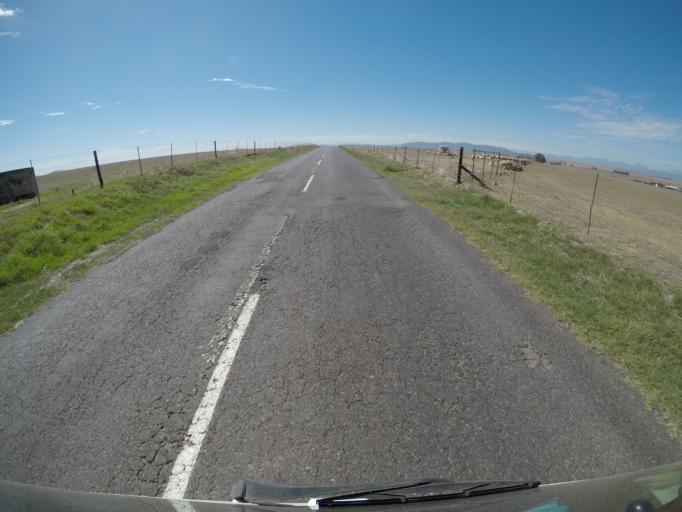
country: ZA
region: Western Cape
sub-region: City of Cape Town
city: Atlantis
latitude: -33.6863
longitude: 18.5985
